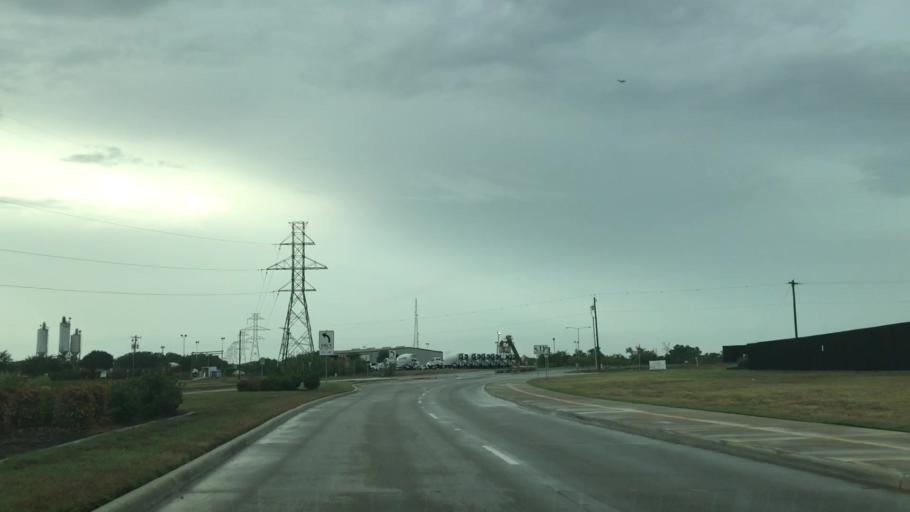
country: US
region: Texas
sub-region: Denton County
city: Lewisville
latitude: 33.0483
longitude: -96.9794
